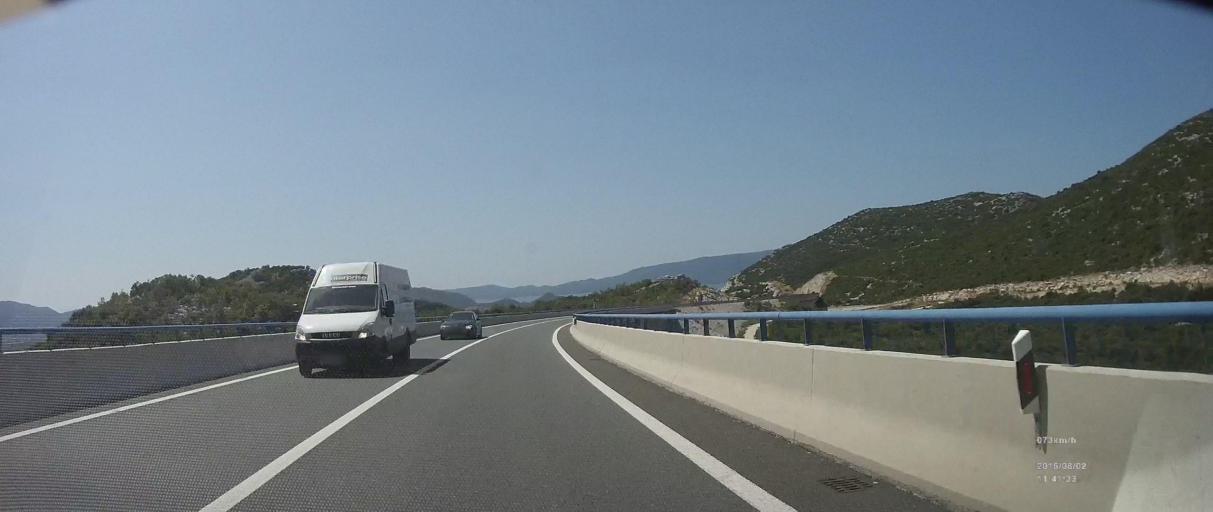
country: HR
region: Dubrovacko-Neretvanska
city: Komin
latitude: 43.0623
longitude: 17.4957
